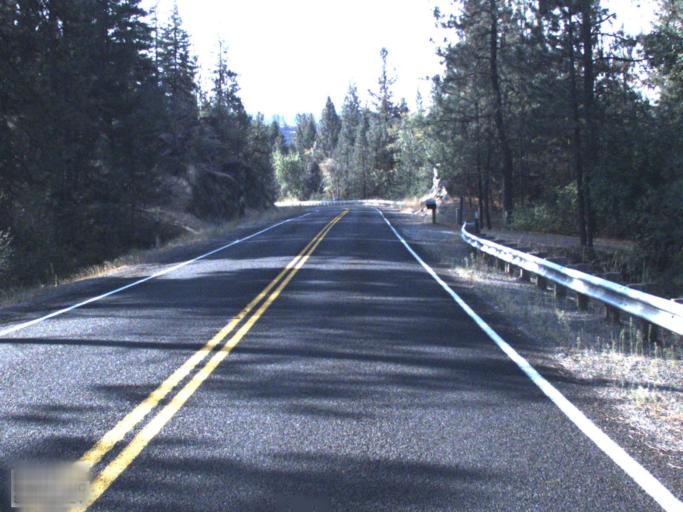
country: US
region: Washington
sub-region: Spokane County
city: Deer Park
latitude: 47.8755
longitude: -117.7085
